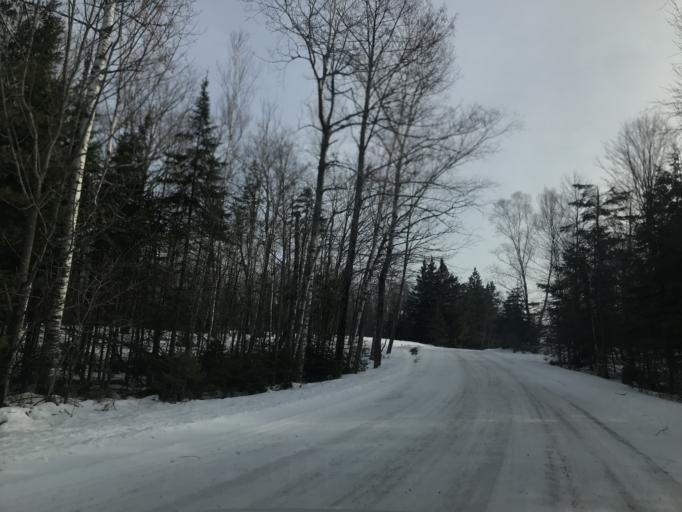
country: US
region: Wisconsin
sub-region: Door County
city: Sturgeon Bay
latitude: 45.1517
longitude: -87.0547
